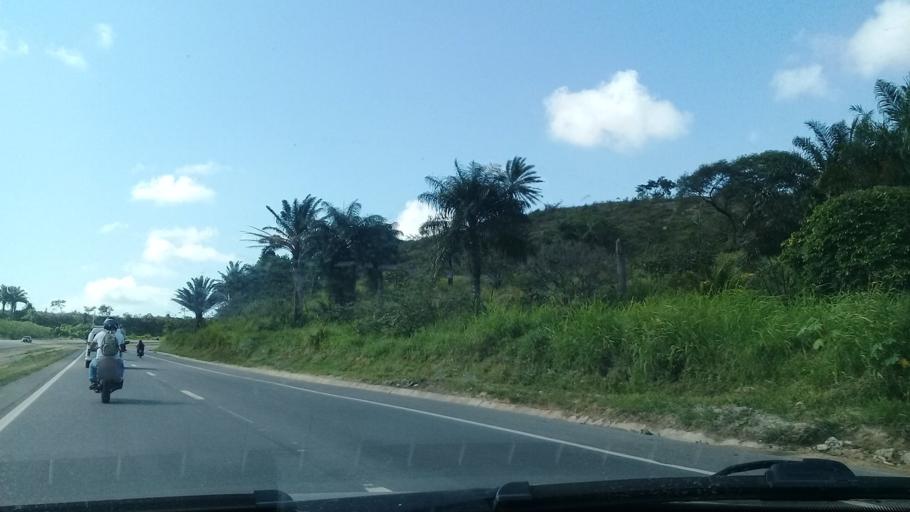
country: BR
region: Pernambuco
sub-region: Jaboatao Dos Guararapes
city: Jaboatao dos Guararapes
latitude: -8.1010
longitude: -34.9495
